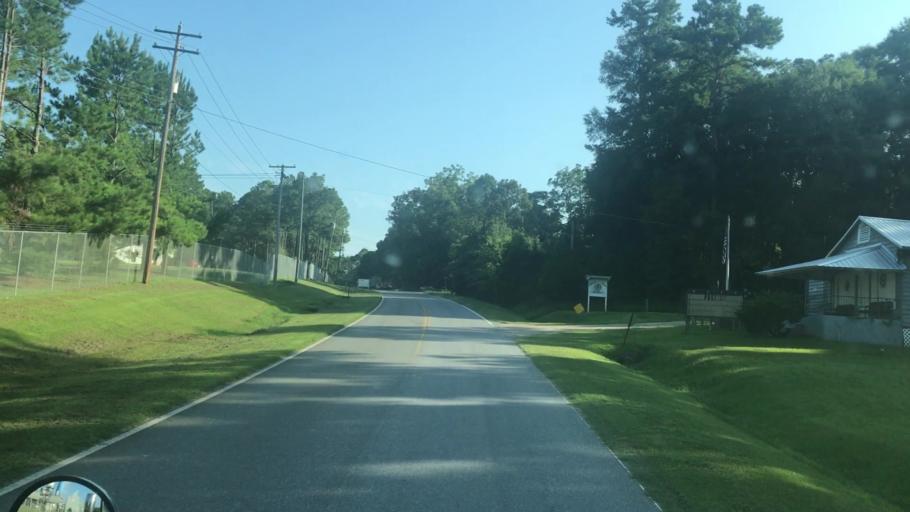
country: US
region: Florida
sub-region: Gadsden County
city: Quincy
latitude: 30.6027
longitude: -84.5723
